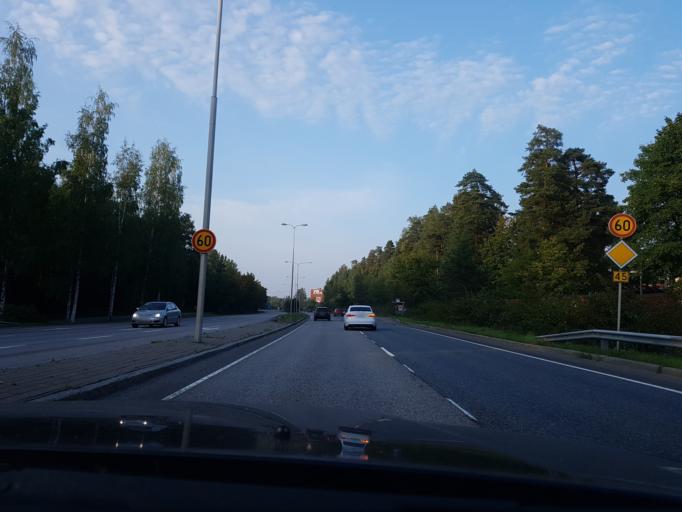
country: FI
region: Uusimaa
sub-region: Helsinki
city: Tuusula
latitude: 60.3792
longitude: 25.0234
